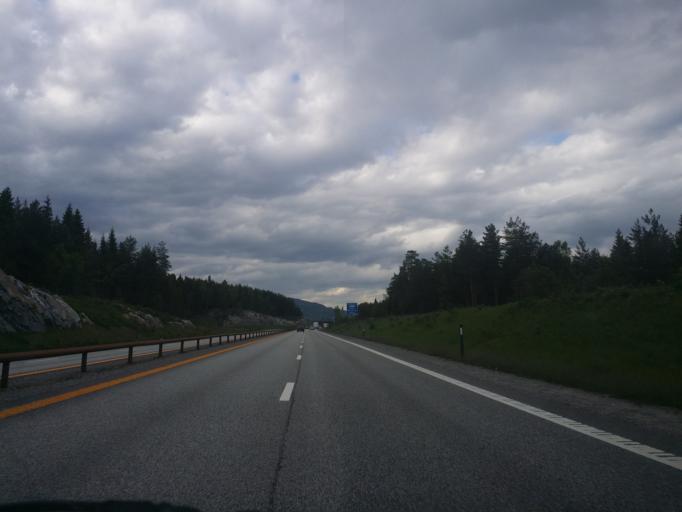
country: NO
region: Akershus
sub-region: Eidsvoll
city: Raholt
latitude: 60.2976
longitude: 11.1379
